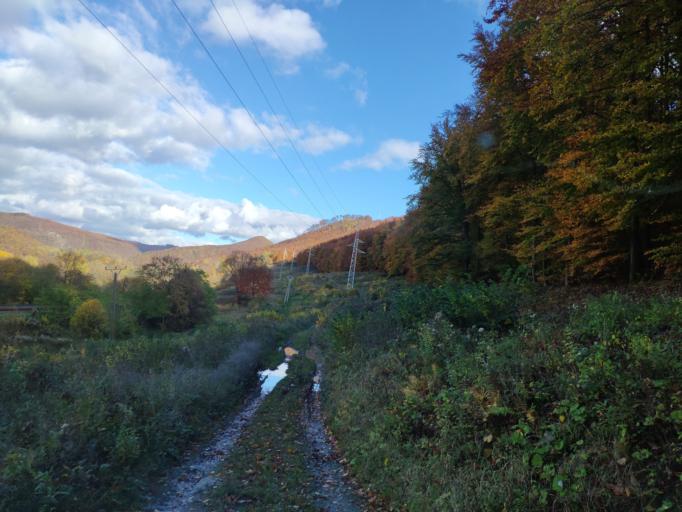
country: SK
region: Presovsky
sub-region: Okres Presov
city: Presov
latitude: 48.8509
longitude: 21.1765
